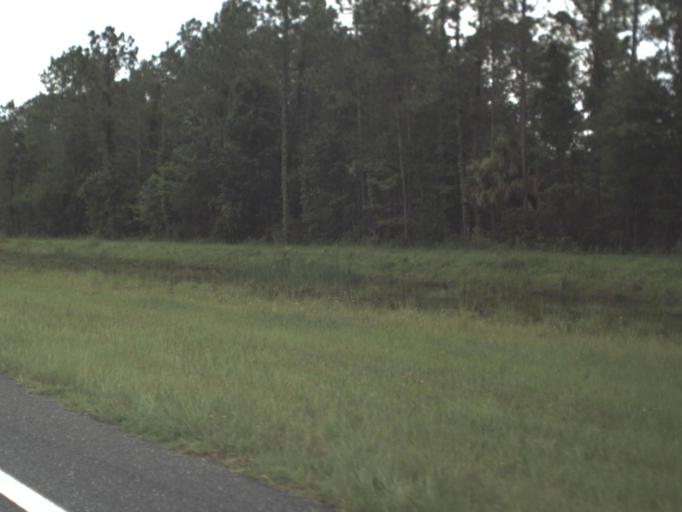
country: US
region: Florida
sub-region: Levy County
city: Chiefland
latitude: 29.3391
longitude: -82.7755
